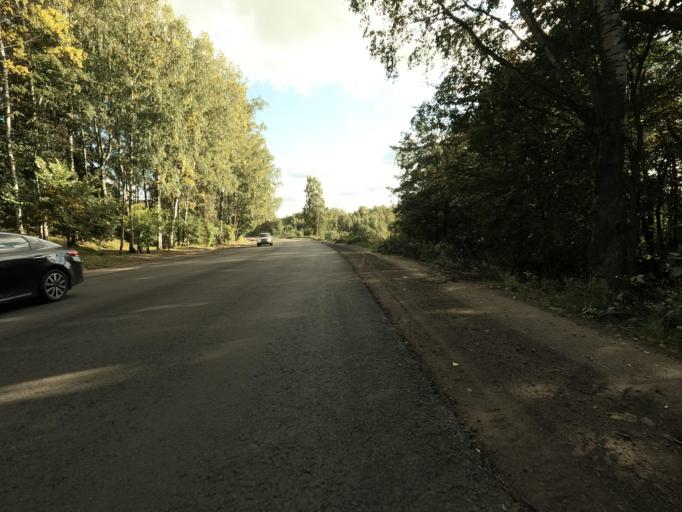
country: RU
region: Leningrad
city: Koltushi
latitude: 59.9426
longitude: 30.6553
